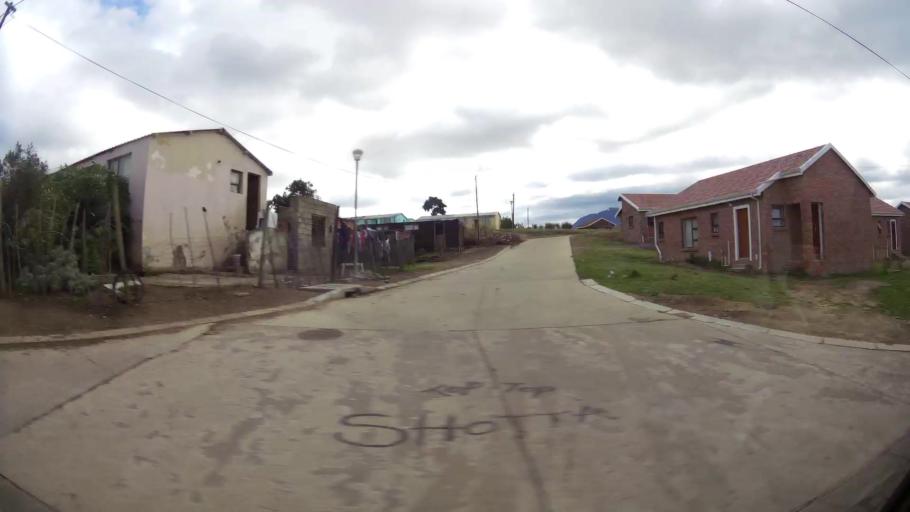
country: ZA
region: Western Cape
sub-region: Eden District Municipality
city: George
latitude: -34.0116
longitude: 22.4574
